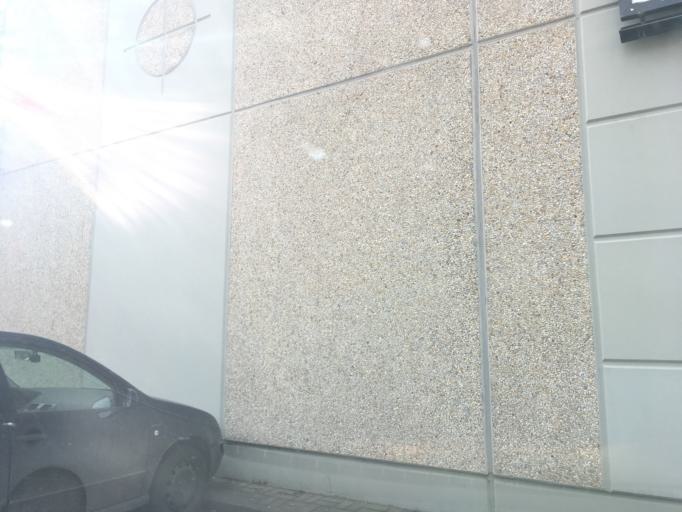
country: PL
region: Pomeranian Voivodeship
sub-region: Slupsk
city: Slupsk
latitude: 54.4714
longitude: 17.0186
